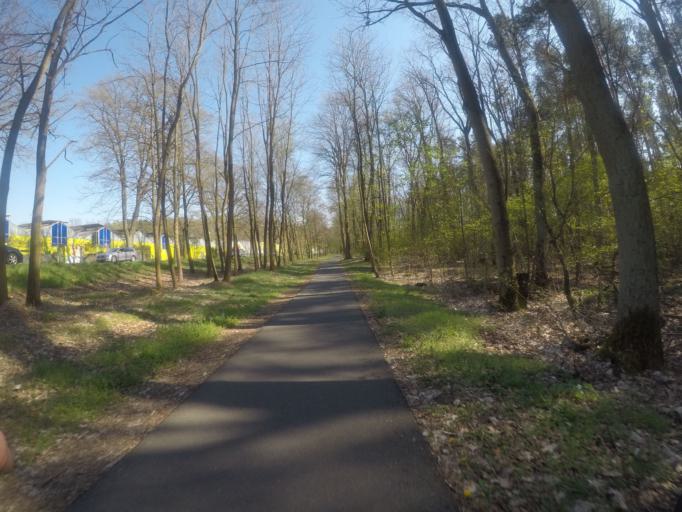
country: DE
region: Brandenburg
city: Birkenwerder
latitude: 52.7085
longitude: 13.2648
